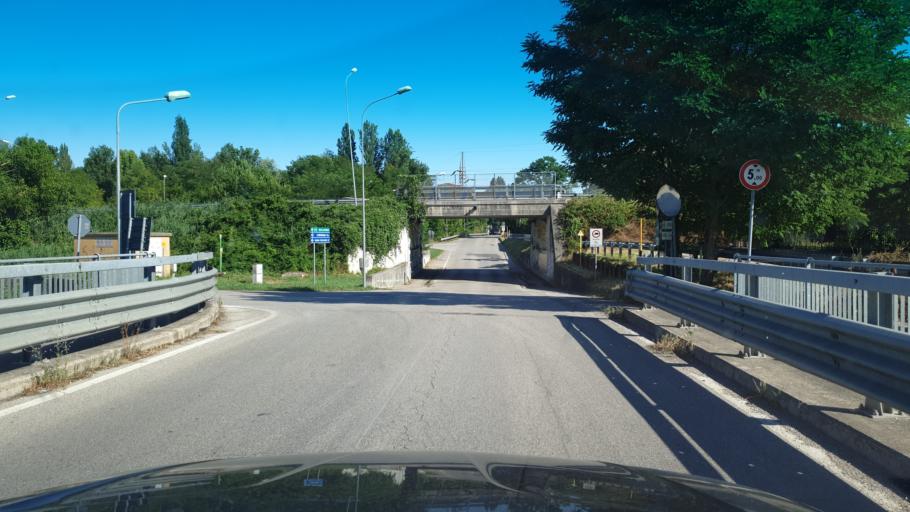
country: IT
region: Veneto
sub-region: Provincia di Rovigo
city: Rovigo
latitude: 45.0825
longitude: 11.7772
